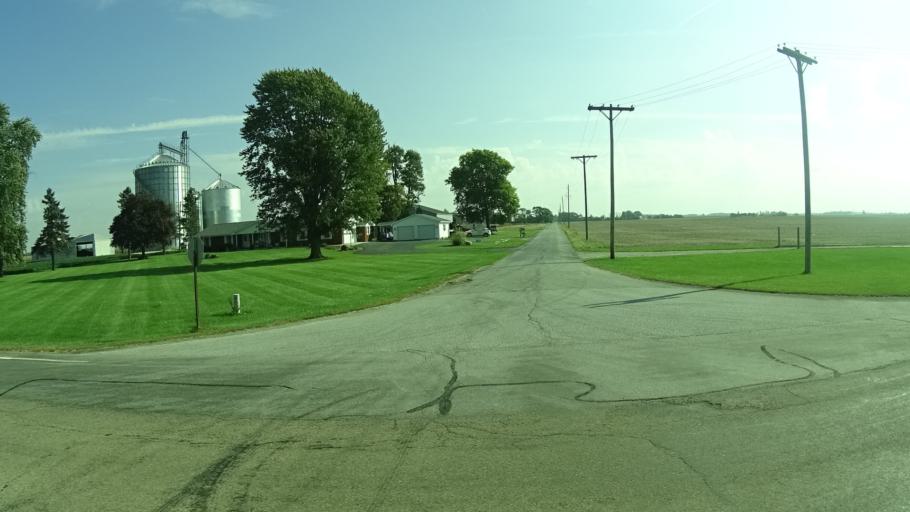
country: US
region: Indiana
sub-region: Madison County
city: Lapel
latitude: 40.0456
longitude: -85.8437
